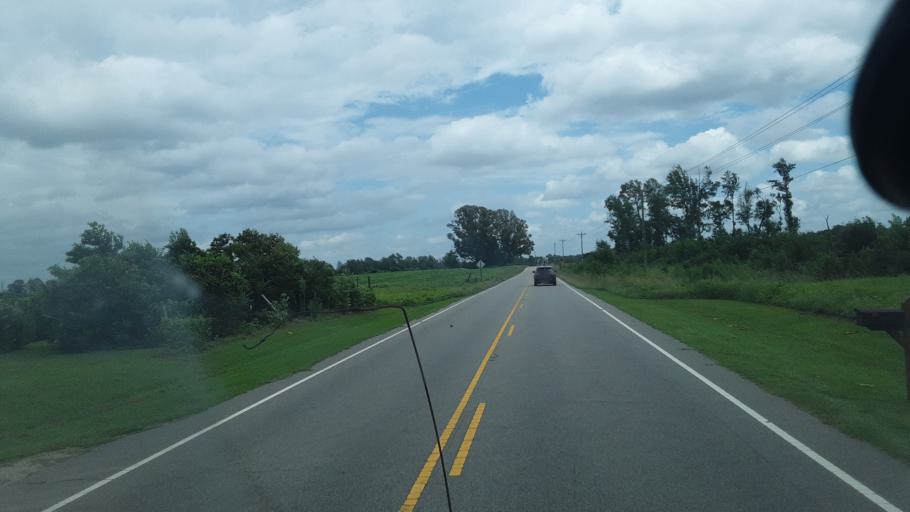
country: US
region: North Carolina
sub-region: Robeson County
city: Rowland
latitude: 34.4755
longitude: -79.2327
